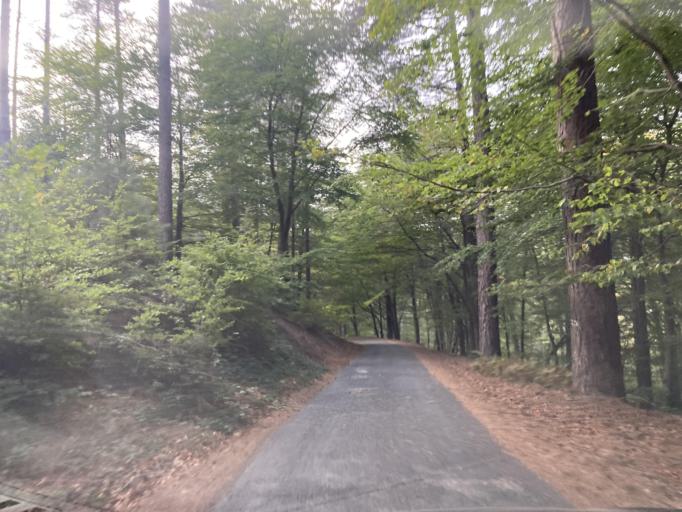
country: FR
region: Languedoc-Roussillon
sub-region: Departement des Pyrenees-Orientales
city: la Roca d'Albera
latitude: 42.4801
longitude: 2.9271
